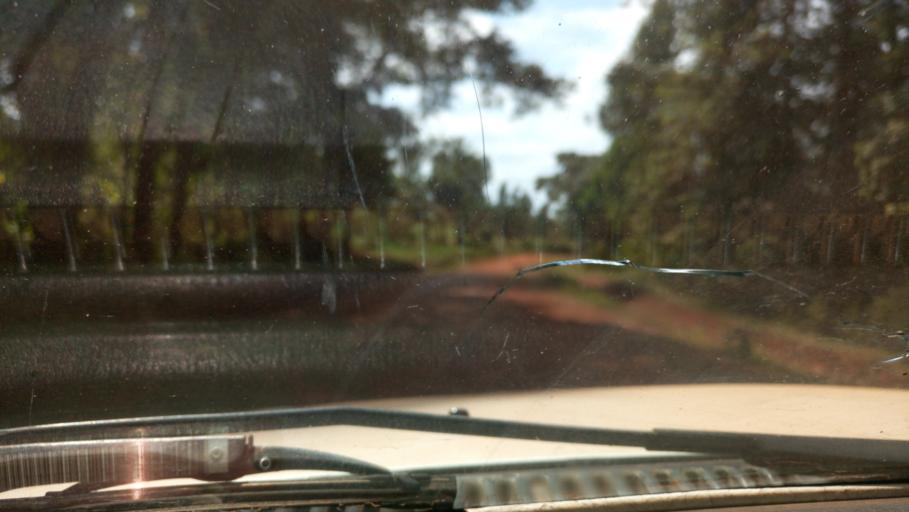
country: KE
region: Murang'a District
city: Maragua
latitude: -0.7656
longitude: 37.1162
